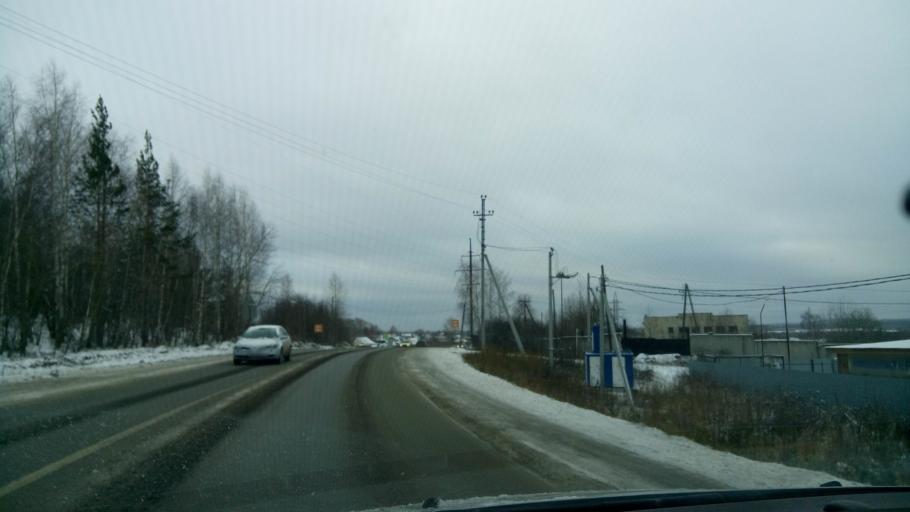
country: RU
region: Sverdlovsk
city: Polevskoy
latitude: 56.4587
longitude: 60.2127
